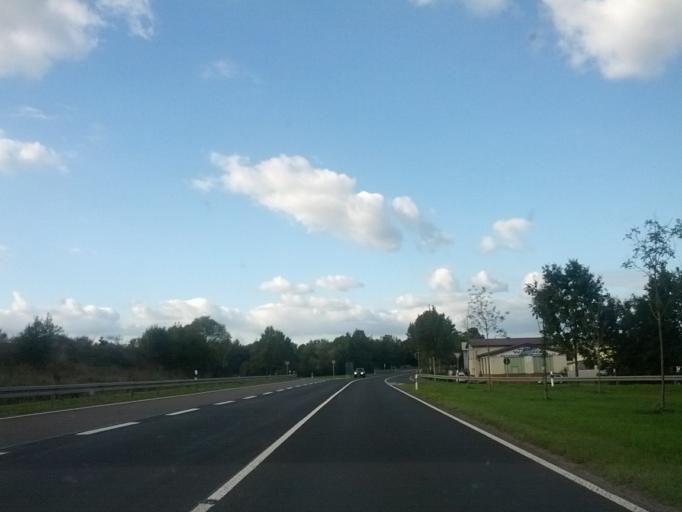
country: DE
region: Thuringia
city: Fambach
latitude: 50.7409
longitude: 10.3576
